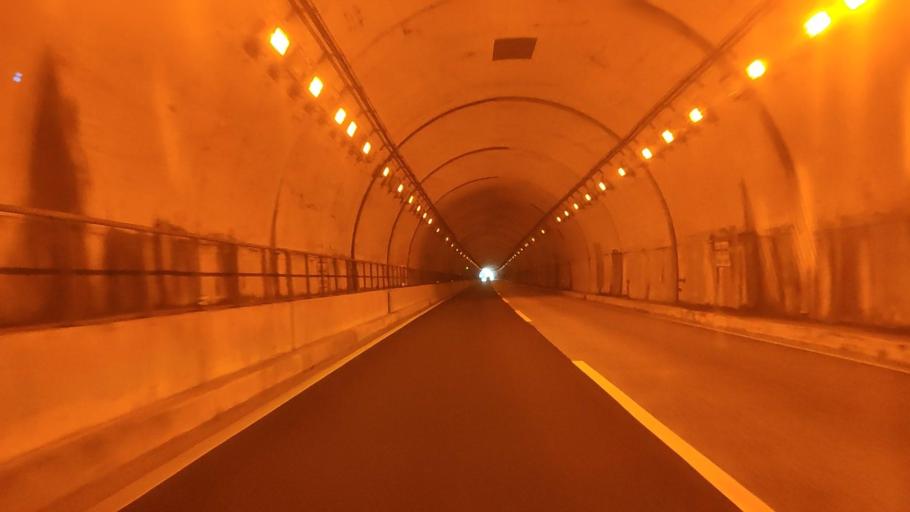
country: JP
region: Miyazaki
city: Miyazaki-shi
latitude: 31.8205
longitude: 131.2582
